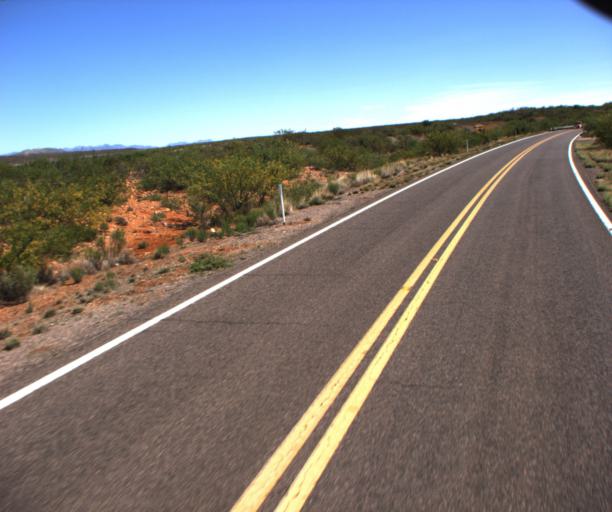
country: US
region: Arizona
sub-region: Cochise County
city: Douglas
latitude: 31.4944
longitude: -109.3366
